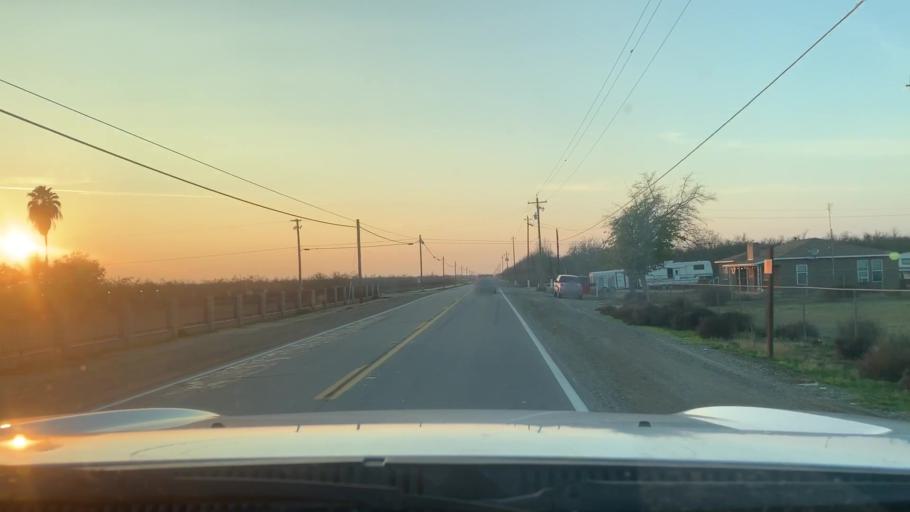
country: US
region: California
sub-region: Kern County
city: Rosedale
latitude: 35.3835
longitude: -119.2155
